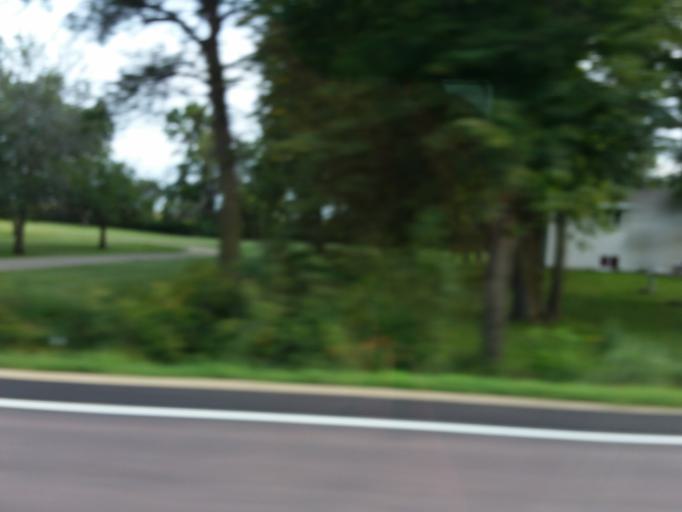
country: US
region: Minnesota
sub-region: Goodhue County
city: Cannon Falls
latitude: 44.6013
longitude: -92.9673
